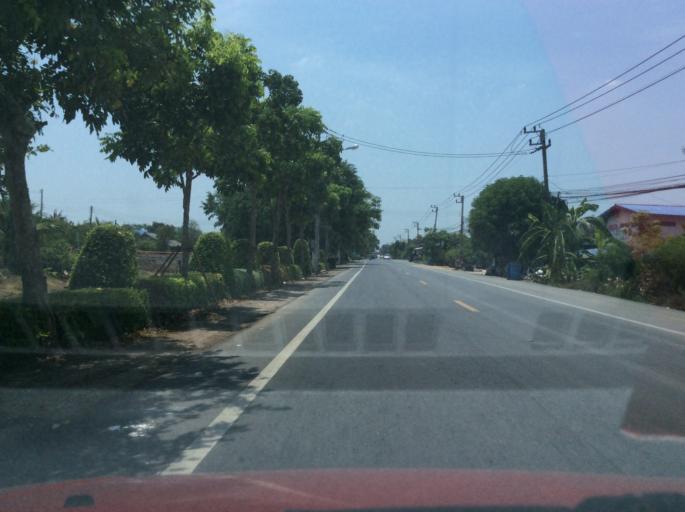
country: TH
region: Pathum Thani
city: Lam Luk Ka
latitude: 13.9555
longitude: 100.7274
